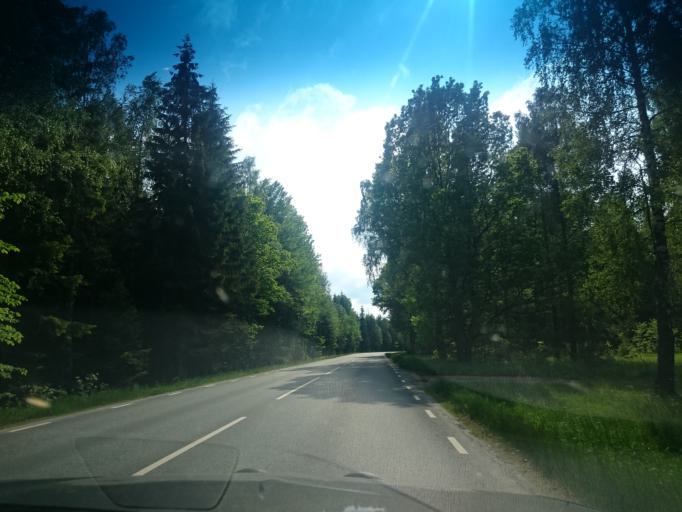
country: SE
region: Joenkoeping
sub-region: Vetlanda Kommun
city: Vetlanda
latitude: 57.4046
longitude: 14.9985
